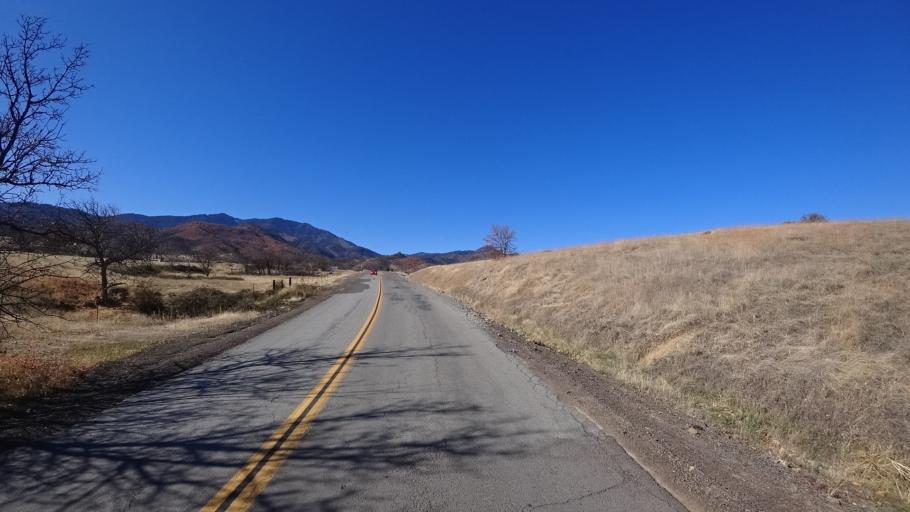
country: US
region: California
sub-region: Siskiyou County
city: Montague
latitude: 41.9201
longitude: -122.5683
